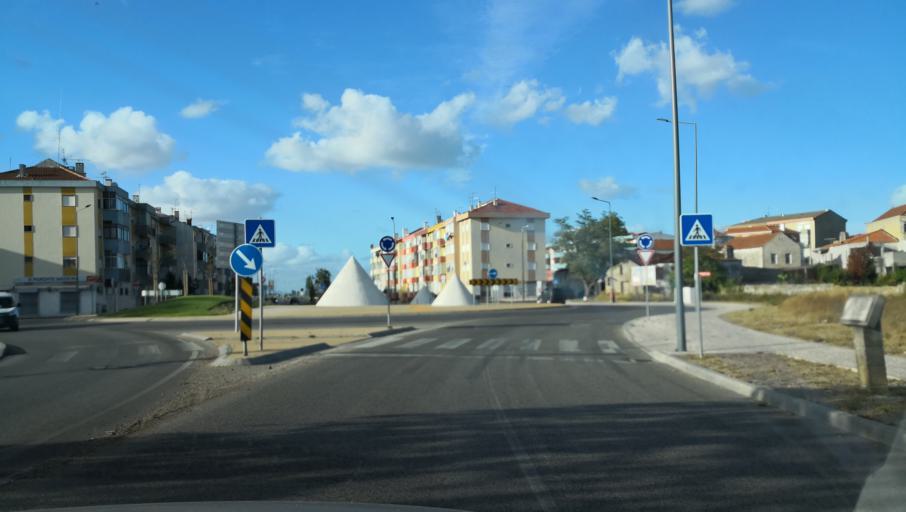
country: PT
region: Setubal
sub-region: Barreiro
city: Barreiro
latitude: 38.6645
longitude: -9.0556
